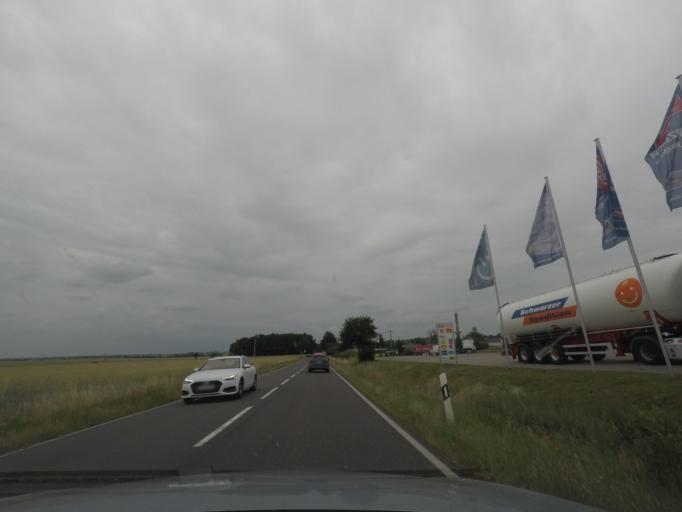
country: DE
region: Saxony-Anhalt
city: Haldensleben I
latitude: 52.2641
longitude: 11.3699
